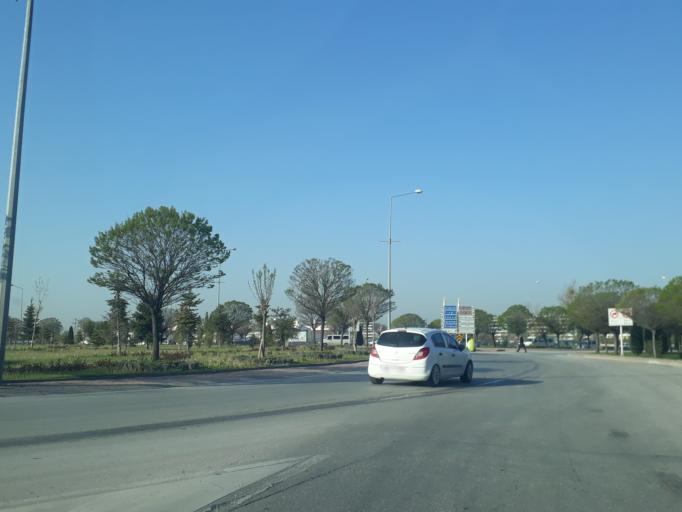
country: TR
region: Konya
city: Selcuklu
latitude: 37.8696
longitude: 32.5479
